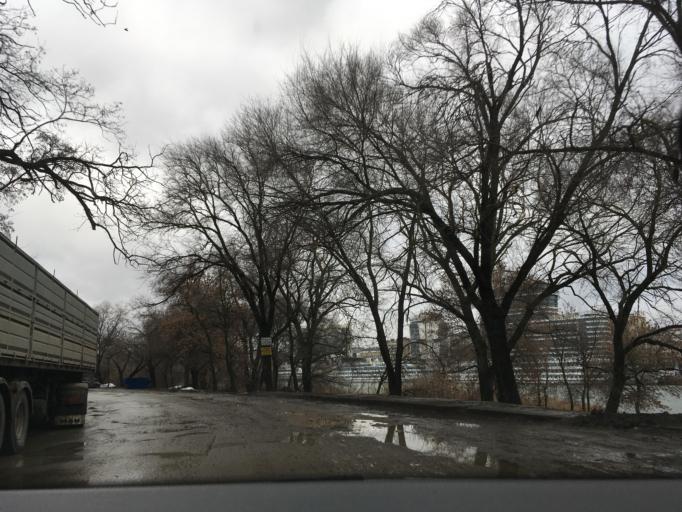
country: RU
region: Rostov
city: Rostov-na-Donu
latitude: 47.2113
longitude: 39.7161
